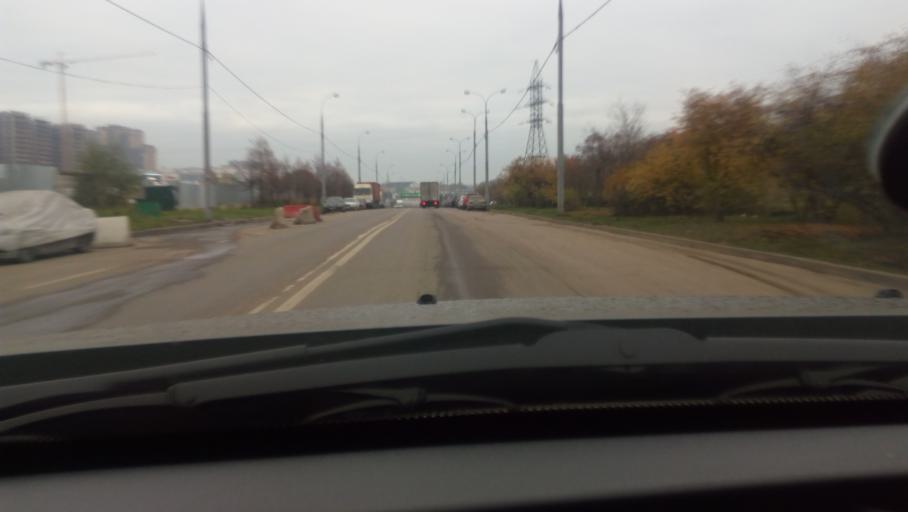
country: RU
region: Moskovskaya
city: Reutov
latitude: 55.7460
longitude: 37.8840
